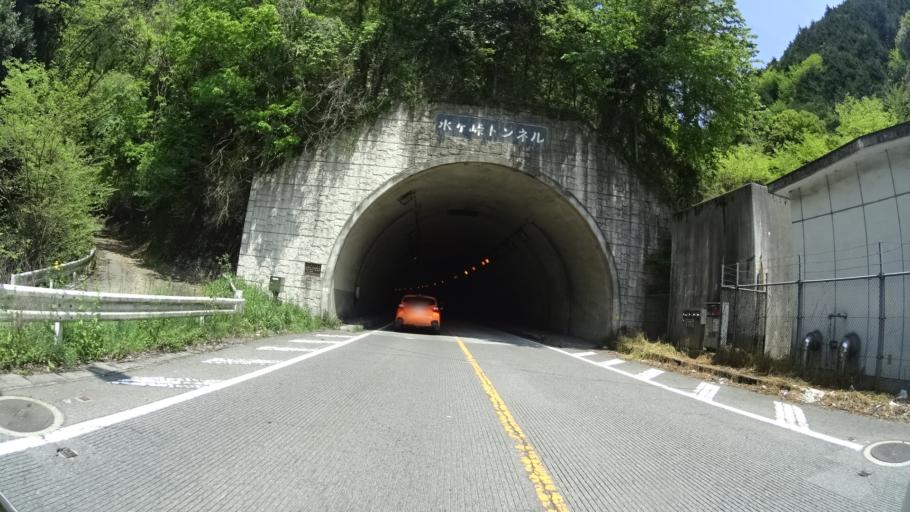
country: JP
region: Ehime
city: Hojo
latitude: 33.9311
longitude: 132.8981
